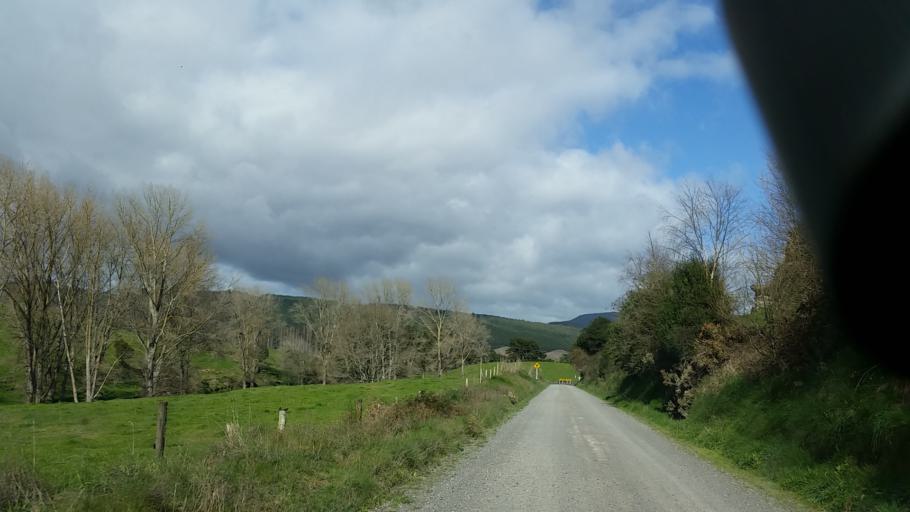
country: NZ
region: Waikato
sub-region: South Waikato District
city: Tokoroa
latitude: -38.3911
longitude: 176.0764
